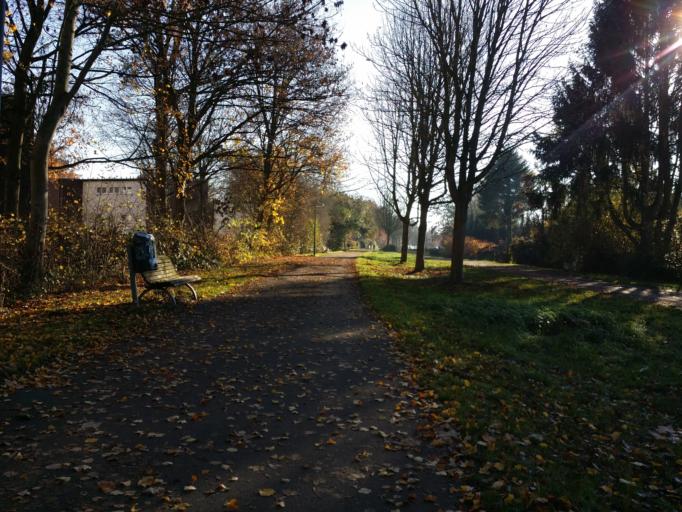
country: DE
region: Bremen
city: Bremen
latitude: 53.0712
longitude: 8.8753
